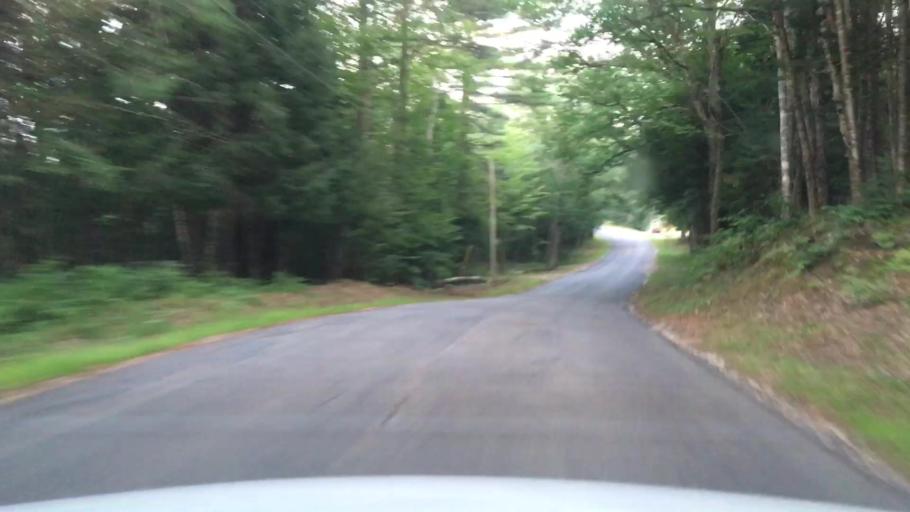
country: US
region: Maine
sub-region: Oxford County
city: Bethel
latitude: 44.4220
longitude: -70.8264
